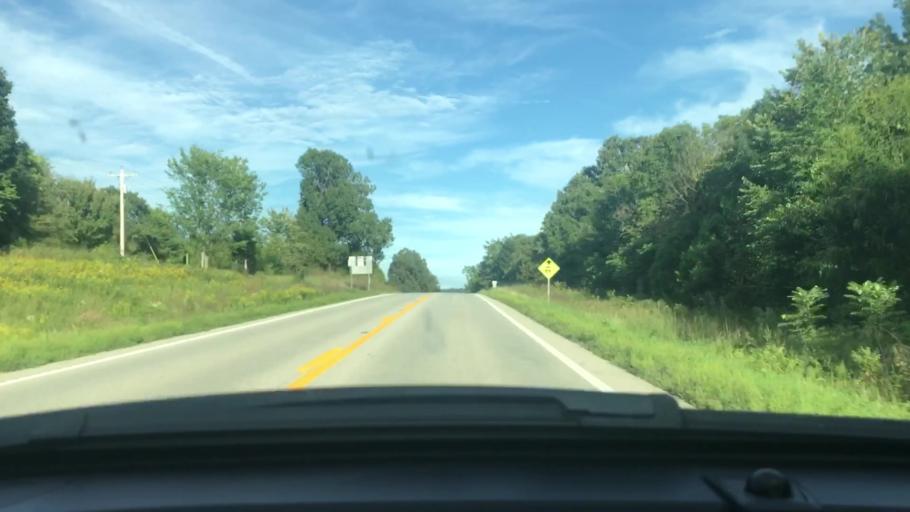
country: US
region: Arkansas
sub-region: Sharp County
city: Cherokee Village
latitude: 36.2744
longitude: -91.3431
